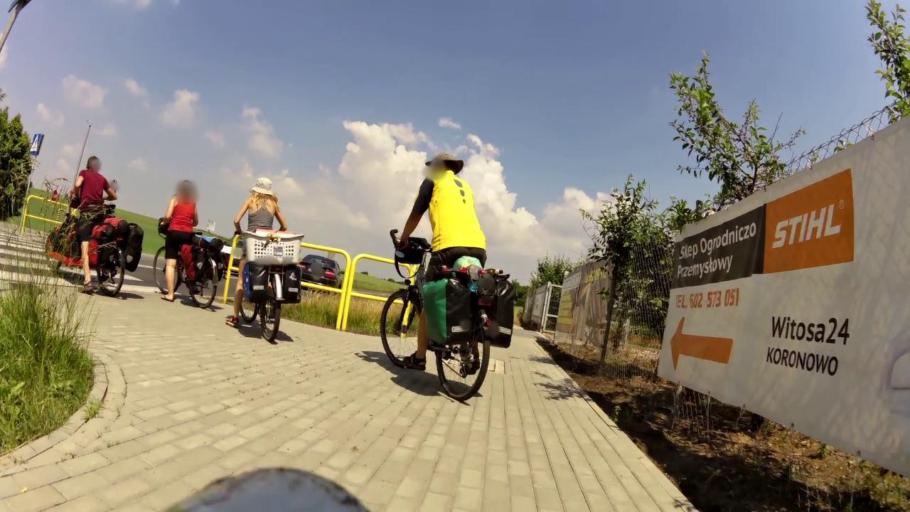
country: PL
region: Kujawsko-Pomorskie
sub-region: Powiat bydgoski
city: Koronowo
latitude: 53.2880
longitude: 17.9327
